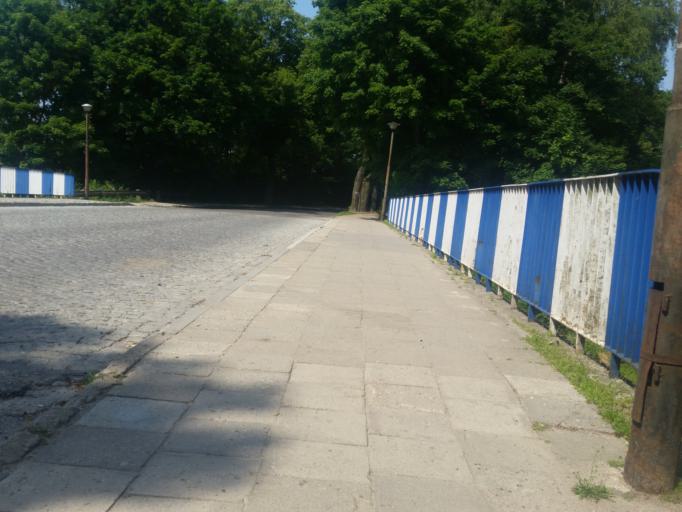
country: PL
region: Warmian-Masurian Voivodeship
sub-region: Powiat goldapski
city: Goldap
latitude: 54.3110
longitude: 22.3061
